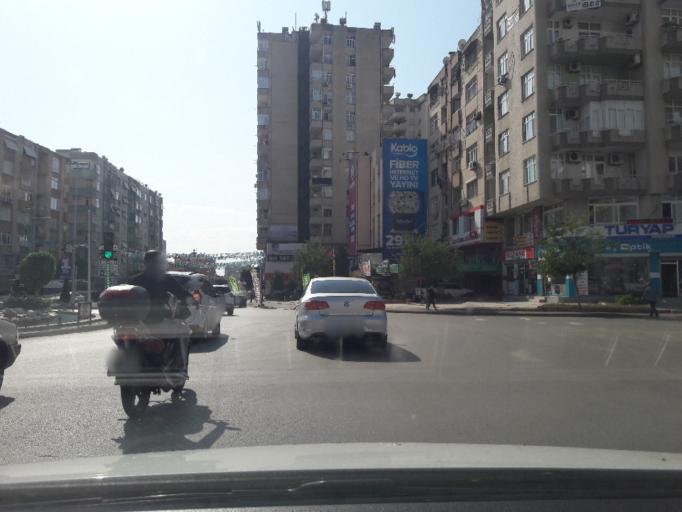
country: TR
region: Adana
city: Adana
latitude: 37.0161
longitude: 35.3220
